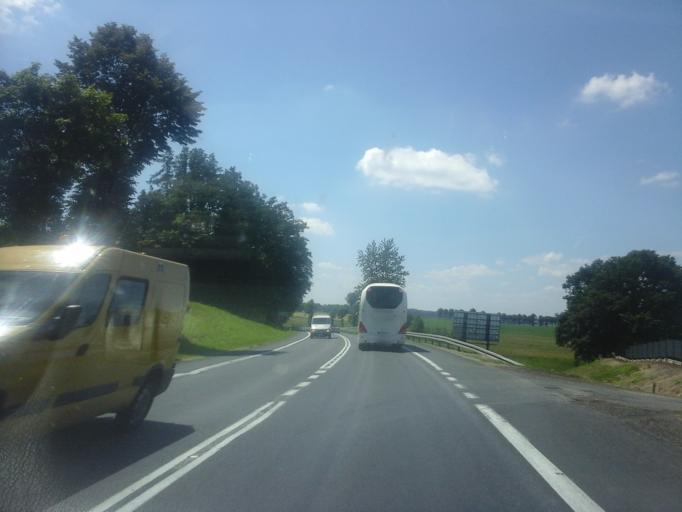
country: PL
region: West Pomeranian Voivodeship
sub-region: Powiat bialogardzki
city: Bialogard
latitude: 54.1262
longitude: 16.0180
